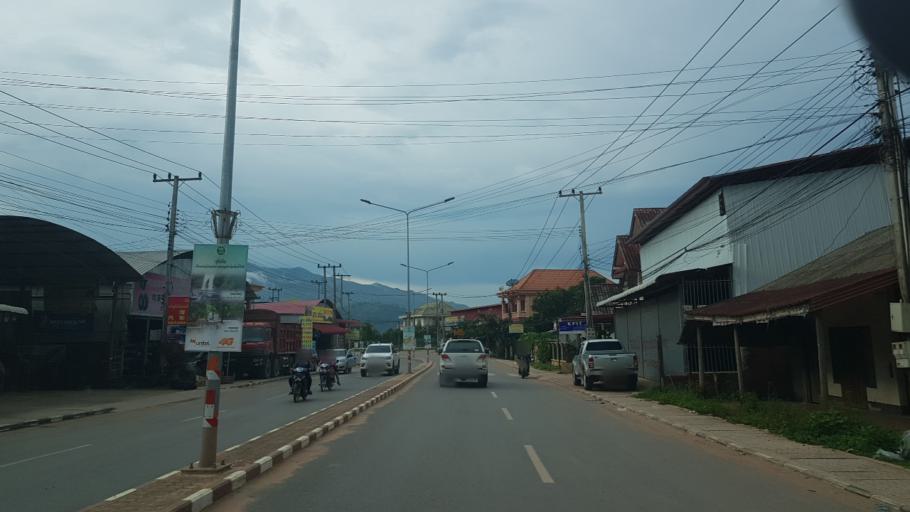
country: LA
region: Oudomxai
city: Muang Xay
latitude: 20.6773
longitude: 101.9865
